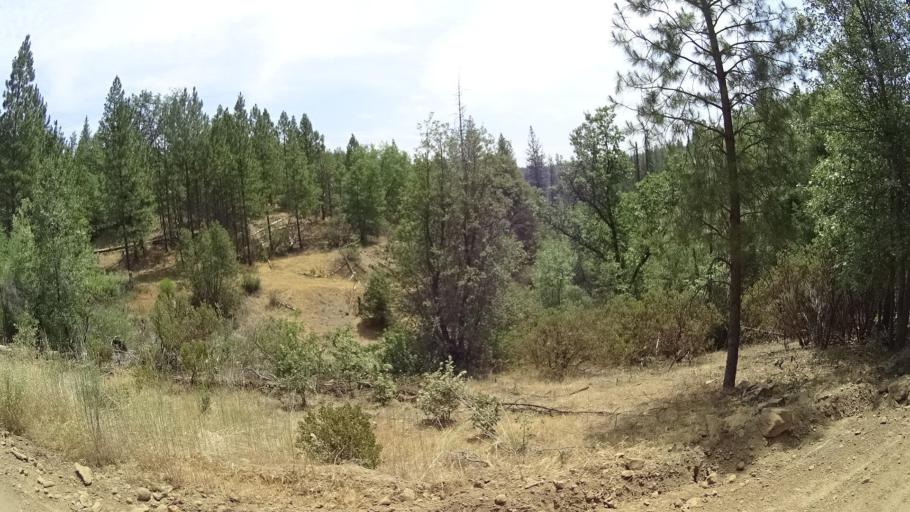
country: US
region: California
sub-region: Mariposa County
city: Midpines
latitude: 37.7463
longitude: -120.0665
